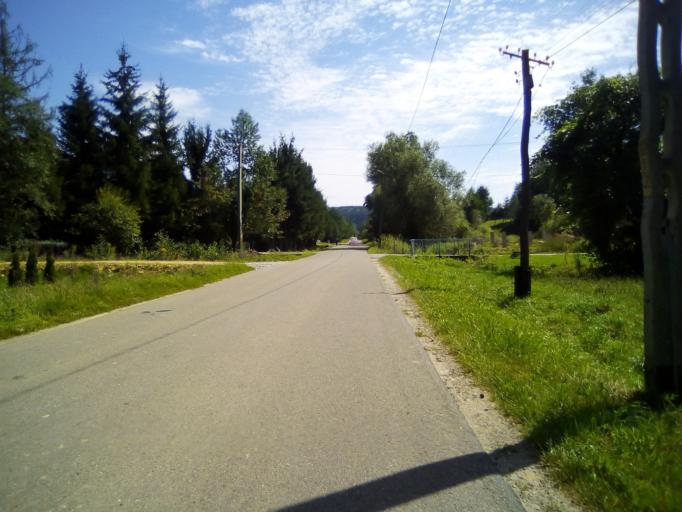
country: PL
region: Subcarpathian Voivodeship
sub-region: Powiat strzyzowski
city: Konieczkowa
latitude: 49.8385
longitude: 21.9291
